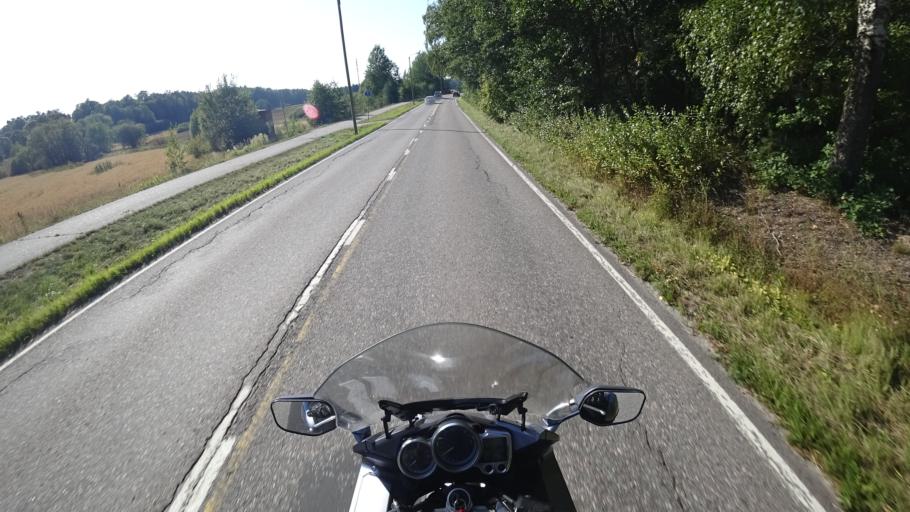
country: FI
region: Uusimaa
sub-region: Helsinki
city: Lohja
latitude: 60.2721
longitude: 24.0169
